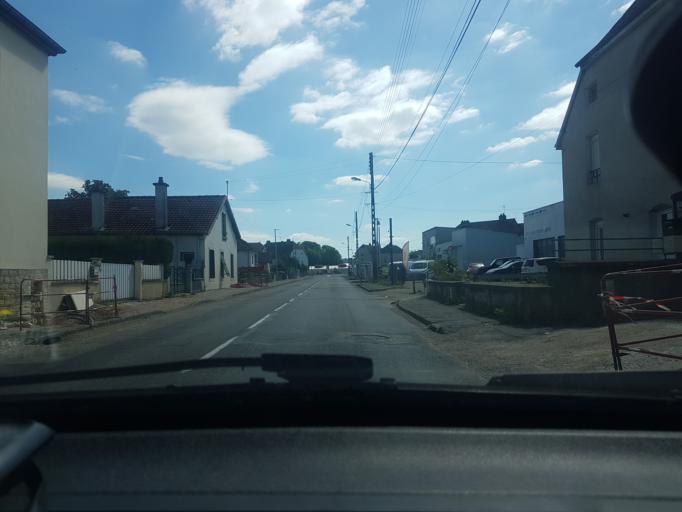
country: FR
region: Franche-Comte
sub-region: Departement de la Haute-Saone
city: Gray
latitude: 47.4424
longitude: 5.5993
